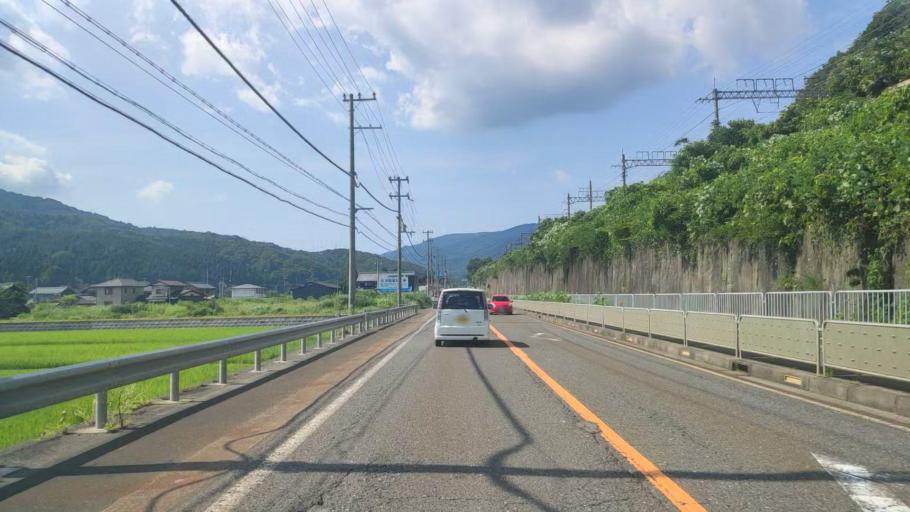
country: JP
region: Fukui
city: Tsuruga
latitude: 35.5353
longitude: 136.1525
